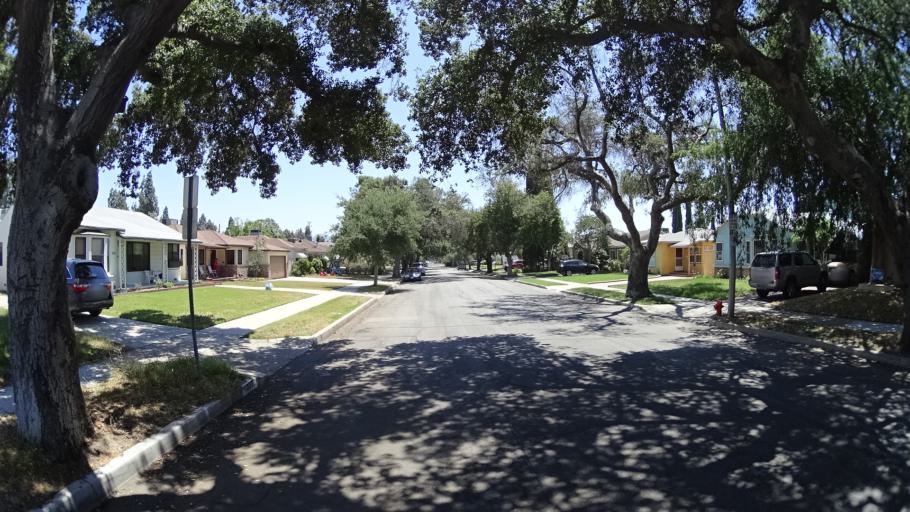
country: US
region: California
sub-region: Los Angeles County
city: Burbank
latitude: 34.1751
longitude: -118.3434
